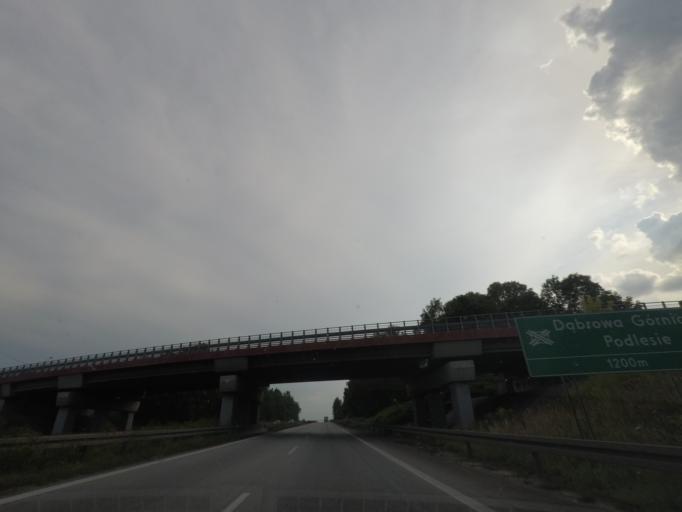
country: PL
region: Silesian Voivodeship
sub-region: Dabrowa Gornicza
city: Dabrowa Gornicza
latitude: 50.3362
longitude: 19.2464
